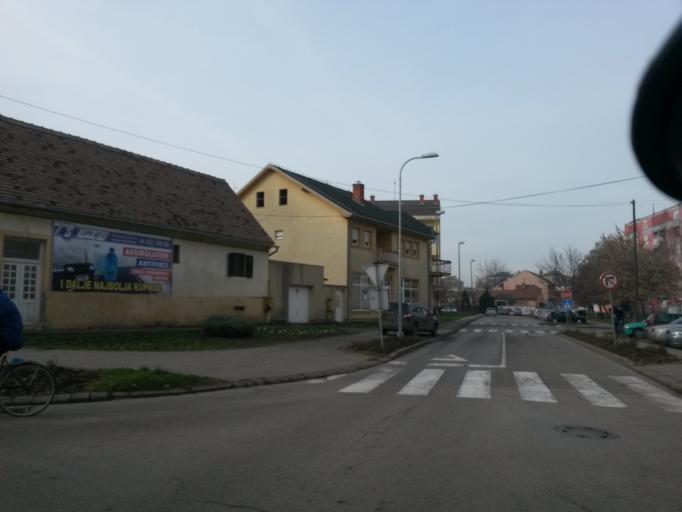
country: HR
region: Vukovarsko-Srijemska
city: Vinkovci
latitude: 45.2925
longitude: 18.8033
